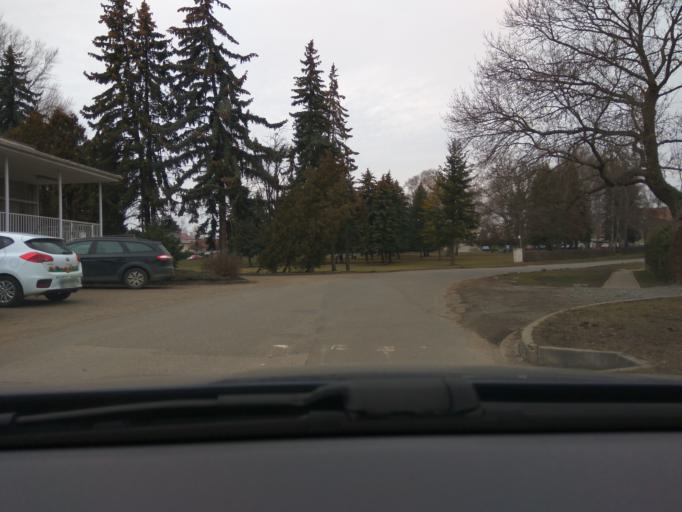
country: CZ
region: Central Bohemia
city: Hovorcovice
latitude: 50.1799
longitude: 14.5187
